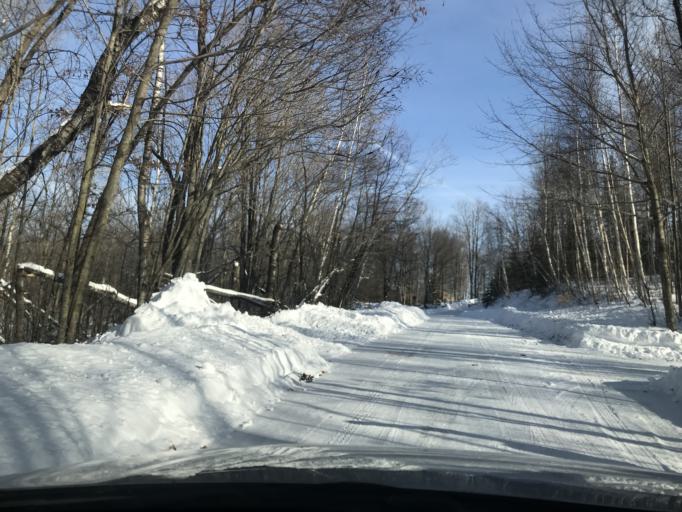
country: US
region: Wisconsin
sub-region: Menominee County
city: Legend Lake
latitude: 45.3274
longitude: -88.5232
